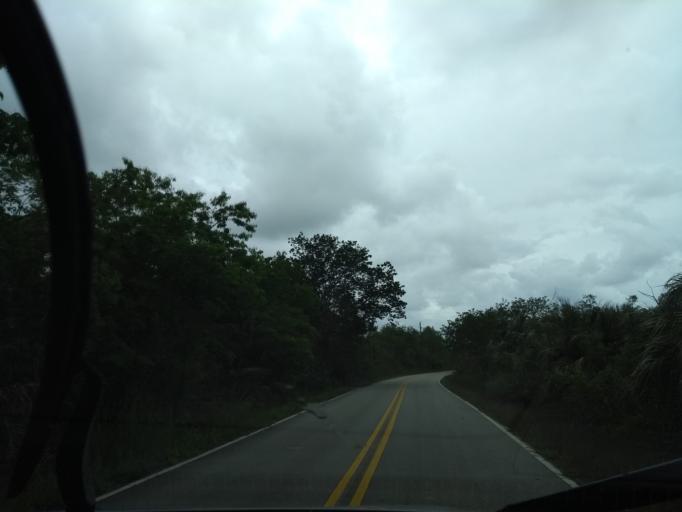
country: US
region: Florida
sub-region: Miami-Dade County
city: The Hammocks
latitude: 25.7464
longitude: -80.9404
